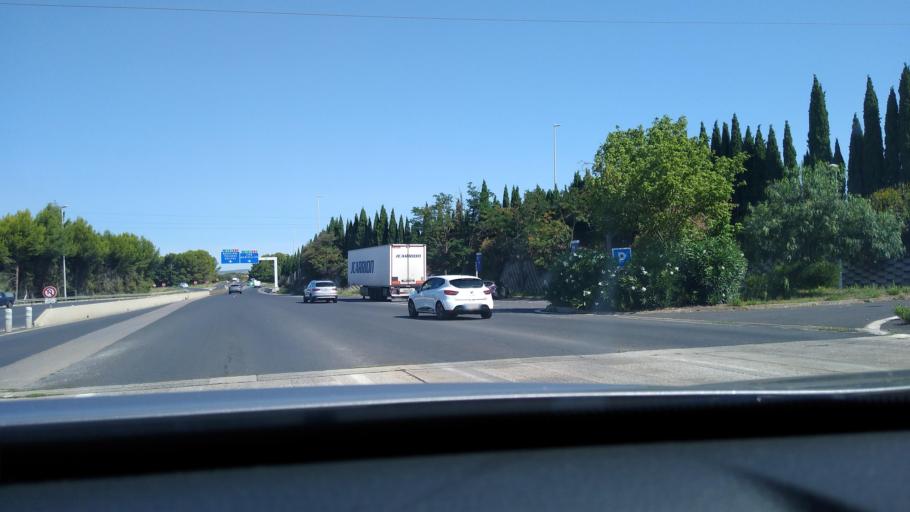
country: FR
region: Languedoc-Roussillon
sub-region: Departement de l'Herault
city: Balaruc-le-Vieux
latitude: 43.4777
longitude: 3.6852
